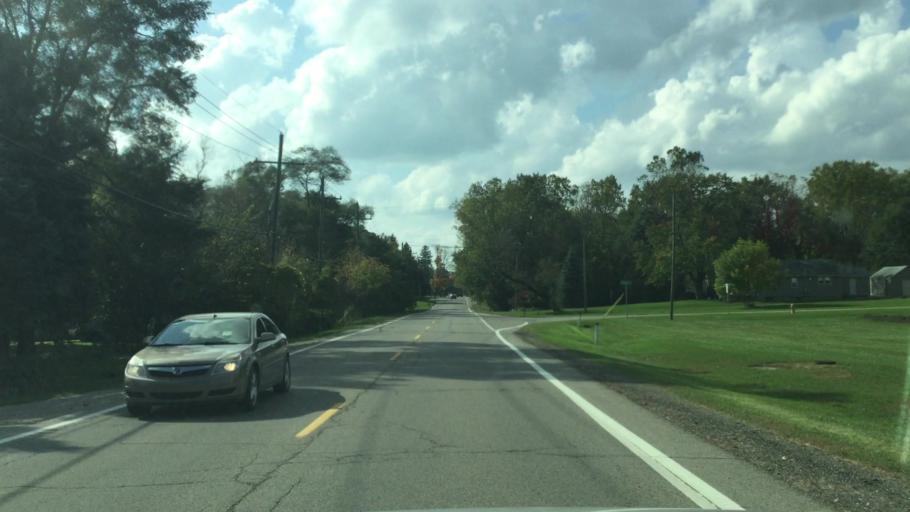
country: US
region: Michigan
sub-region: Oakland County
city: Waterford
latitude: 42.6525
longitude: -83.4096
